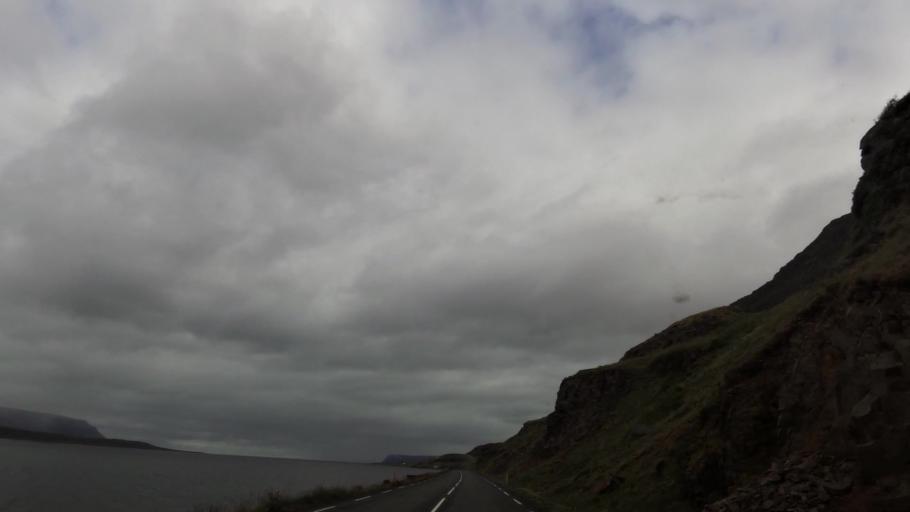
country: IS
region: Westfjords
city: Isafjoerdur
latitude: 65.9865
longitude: -22.7754
